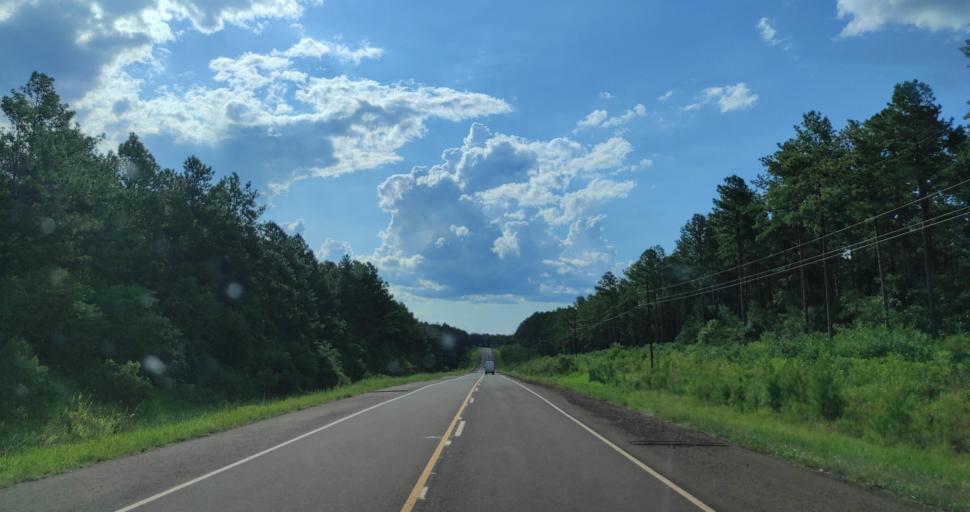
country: AR
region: Misiones
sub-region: Departamento de San Pedro
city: San Pedro
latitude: -26.3517
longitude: -53.9639
